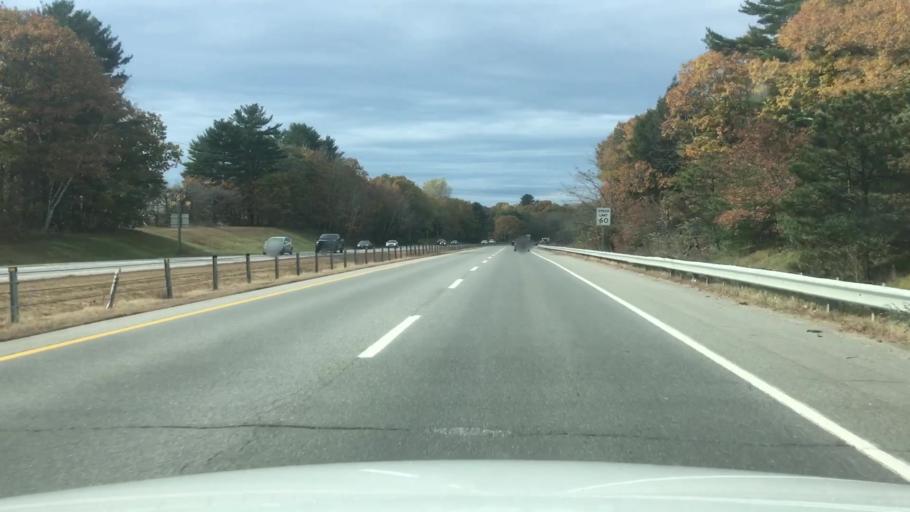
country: US
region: Maine
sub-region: Cumberland County
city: Brunswick
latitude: 43.9095
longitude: -69.9216
